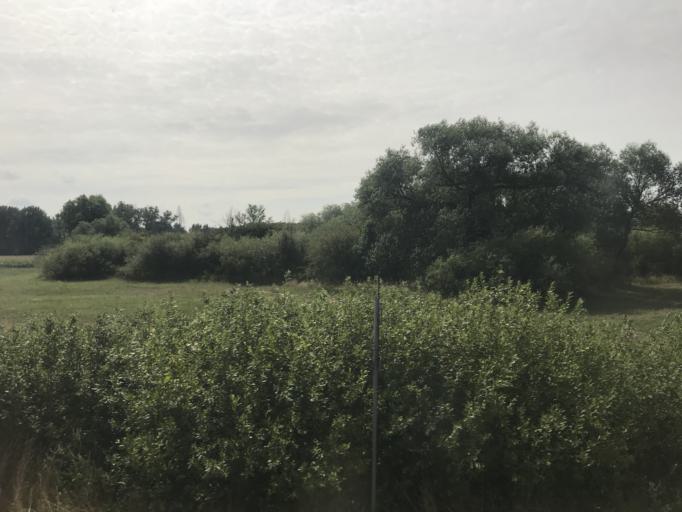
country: PL
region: Kujawsko-Pomorskie
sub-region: Powiat inowroclawski
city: Janikowo
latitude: 52.7777
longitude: 18.1668
